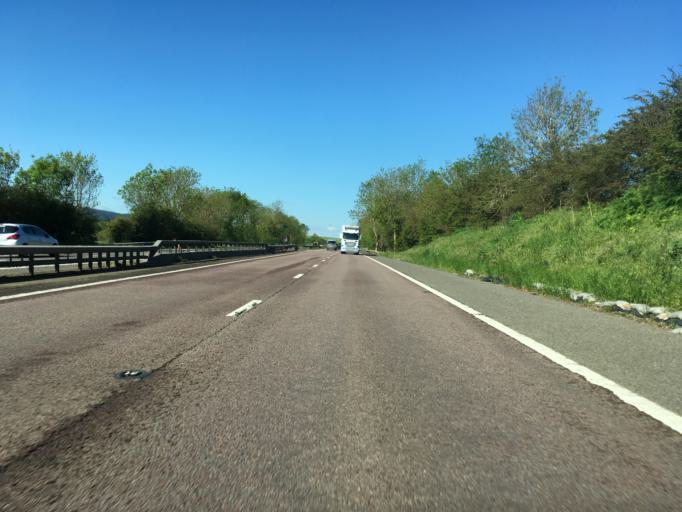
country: GB
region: England
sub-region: Herefordshire
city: Linton
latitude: 51.9312
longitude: -2.5214
